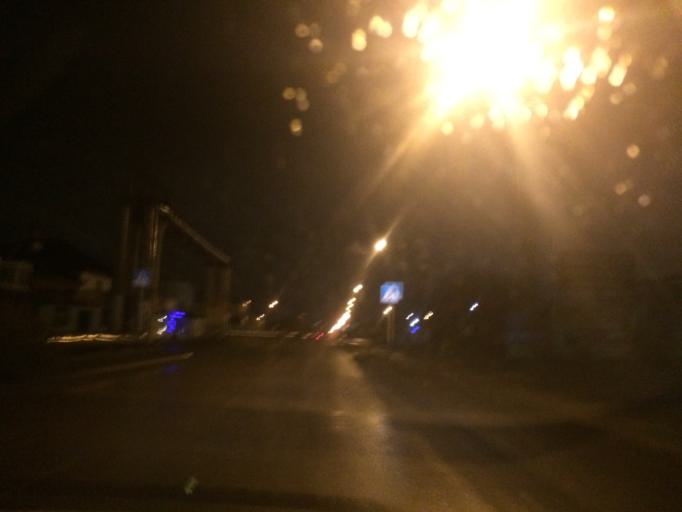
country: KZ
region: Astana Qalasy
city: Astana
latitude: 51.1822
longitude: 71.3856
